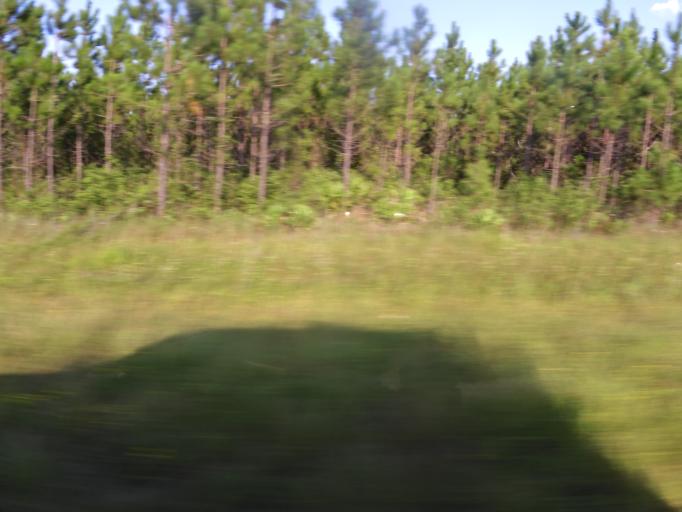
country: US
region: Florida
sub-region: Duval County
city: Baldwin
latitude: 30.3587
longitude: -82.0095
